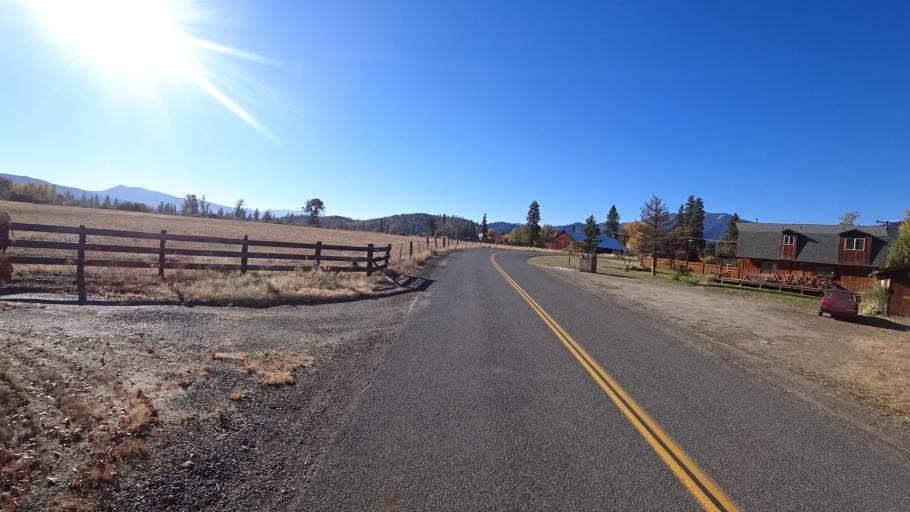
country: US
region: California
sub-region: Siskiyou County
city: Yreka
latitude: 41.4640
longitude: -122.8838
